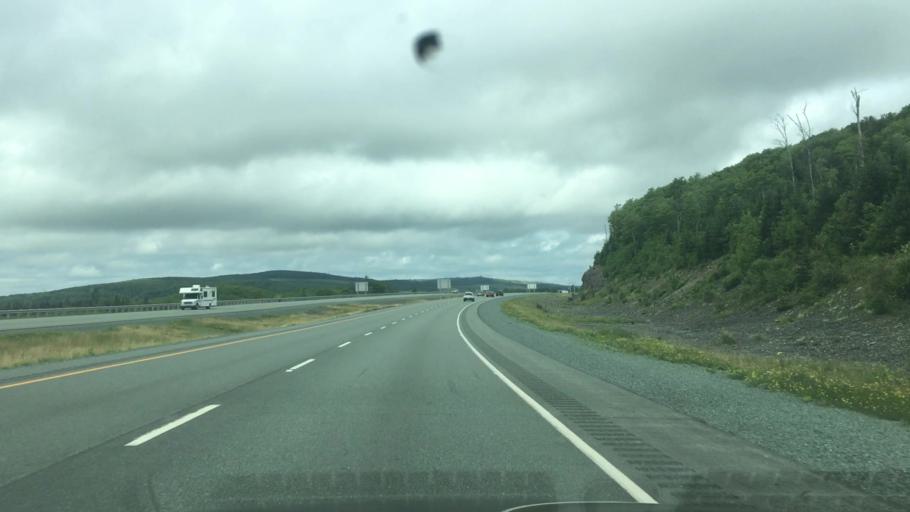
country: CA
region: Nova Scotia
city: Oxford
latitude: 45.5292
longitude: -63.7087
